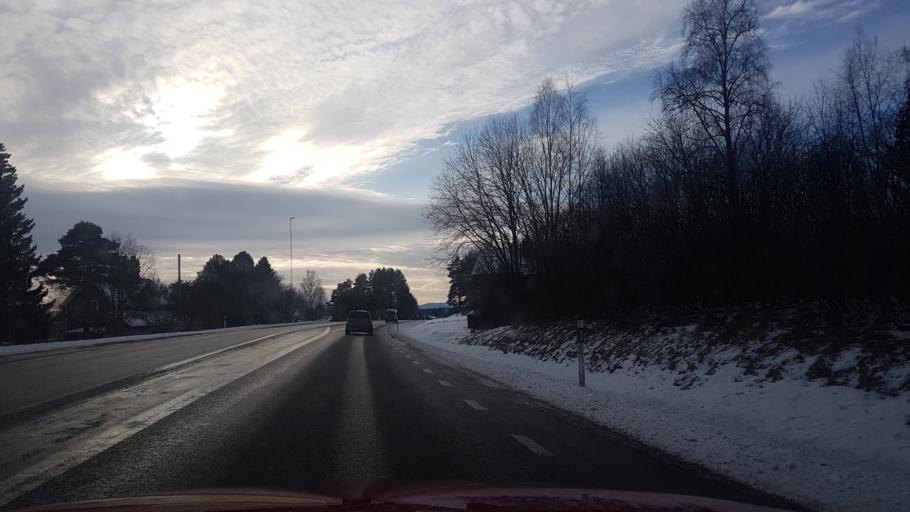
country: SE
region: Dalarna
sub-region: Rattviks Kommun
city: Vikarbyn
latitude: 60.9093
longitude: 15.0073
